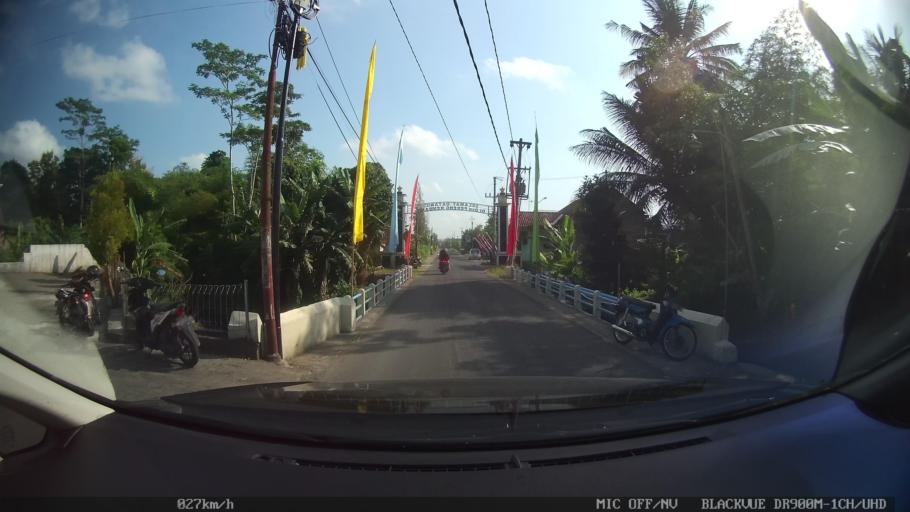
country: ID
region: Daerah Istimewa Yogyakarta
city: Gamping Lor
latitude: -7.8120
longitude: 110.2992
